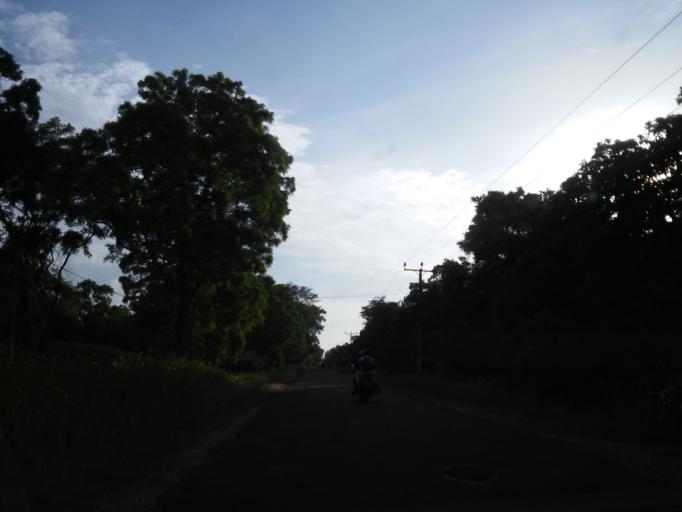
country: LK
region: Central
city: Sigiriya
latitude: 8.1743
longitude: 80.6662
